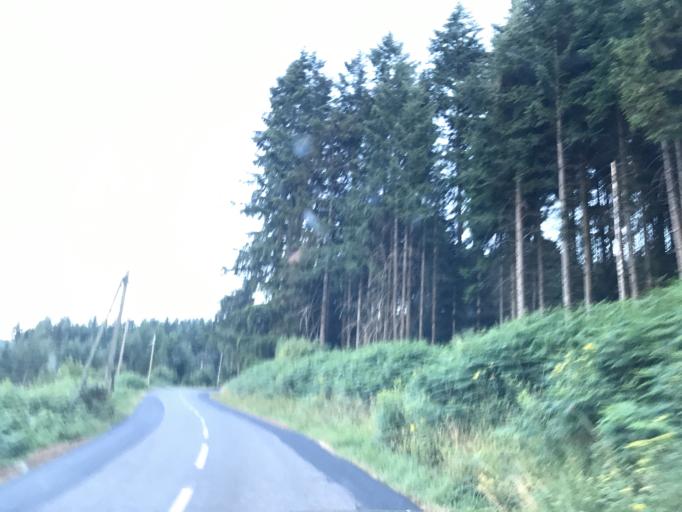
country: FR
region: Auvergne
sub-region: Departement du Puy-de-Dome
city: Chabreloche
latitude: 45.8286
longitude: 3.6908
